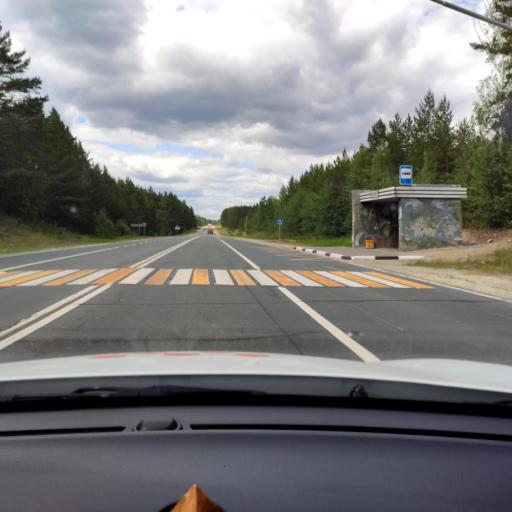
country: RU
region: Mariy-El
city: Krasnogorskiy
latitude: 56.0766
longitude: 48.3590
